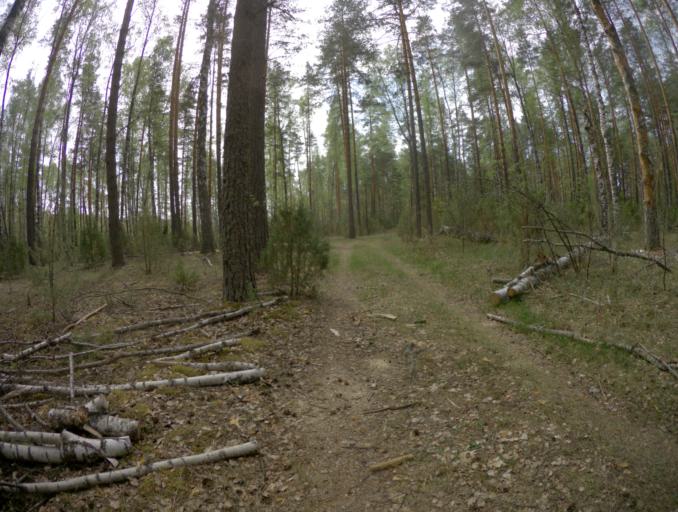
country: RU
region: Ivanovo
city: Yuzha
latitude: 56.4894
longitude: 42.1606
